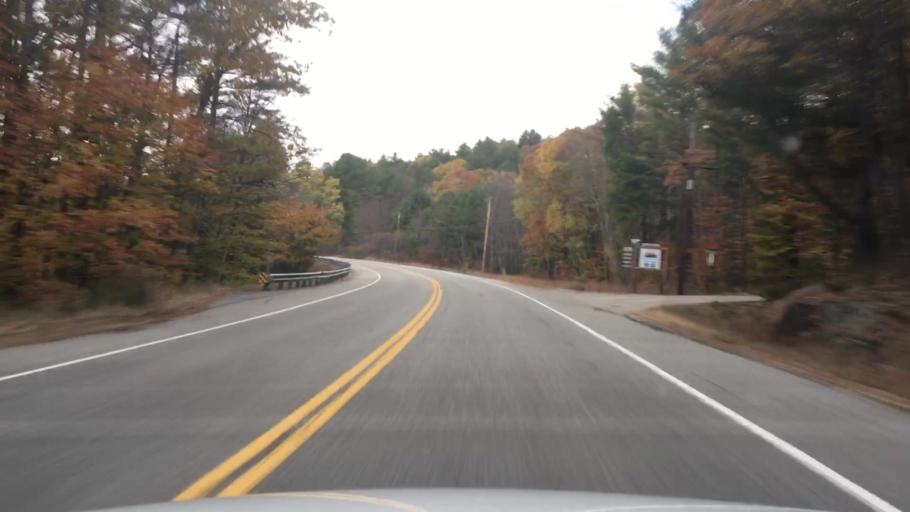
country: US
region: Maine
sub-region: Androscoggin County
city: Livermore
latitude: 44.4036
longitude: -70.2647
